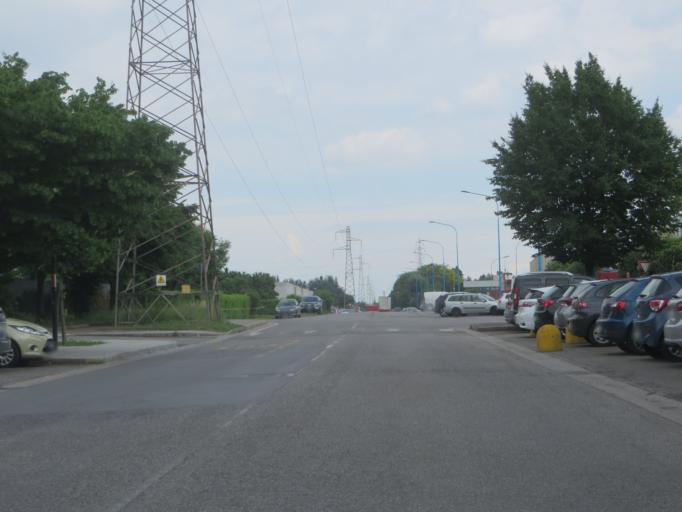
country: IT
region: Lombardy
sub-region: Provincia di Brescia
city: Roncadelle
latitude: 45.5190
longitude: 10.1592
